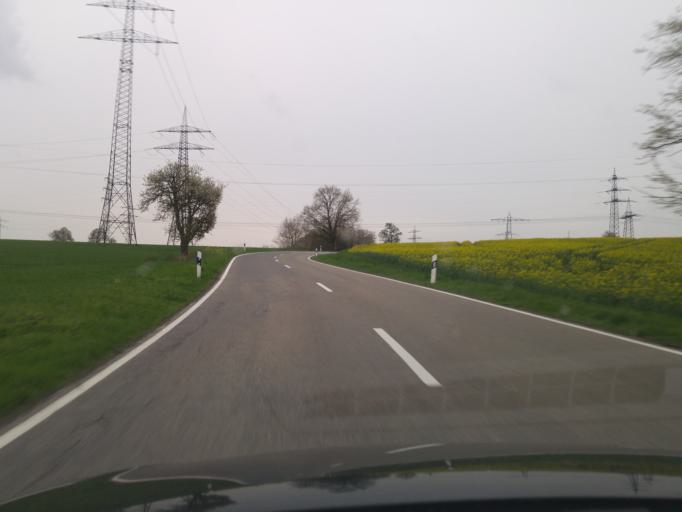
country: DE
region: Baden-Wuerttemberg
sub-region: Karlsruhe Region
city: Huffenhardt
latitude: 49.2934
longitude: 9.1016
